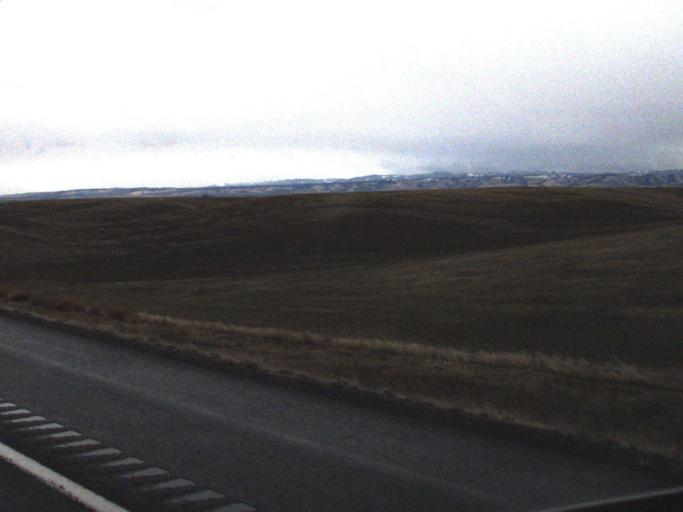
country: US
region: Washington
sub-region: Walla Walla County
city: Garrett
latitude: 46.0617
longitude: -118.4309
